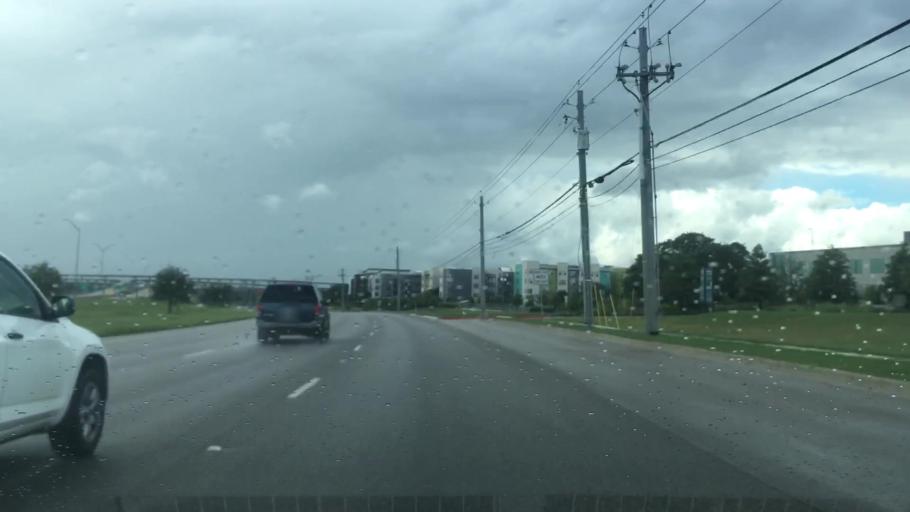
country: US
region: Texas
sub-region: Williamson County
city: Jollyville
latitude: 30.4755
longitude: -97.7766
